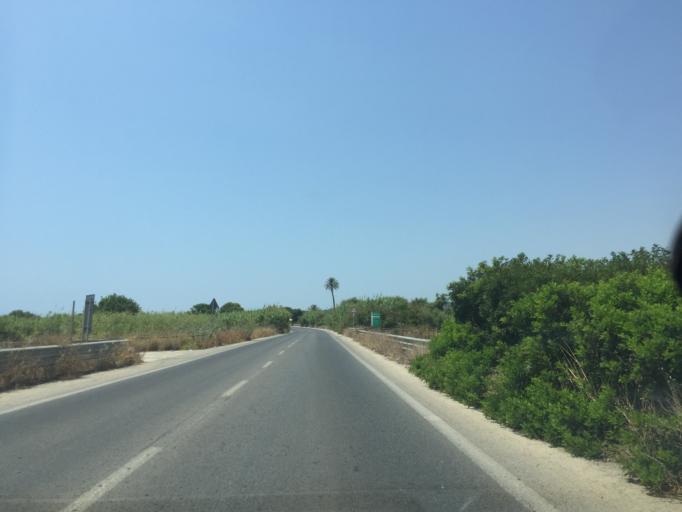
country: IT
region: Sicily
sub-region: Ragusa
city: Marina di Ragusa
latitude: 36.7777
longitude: 14.5969
